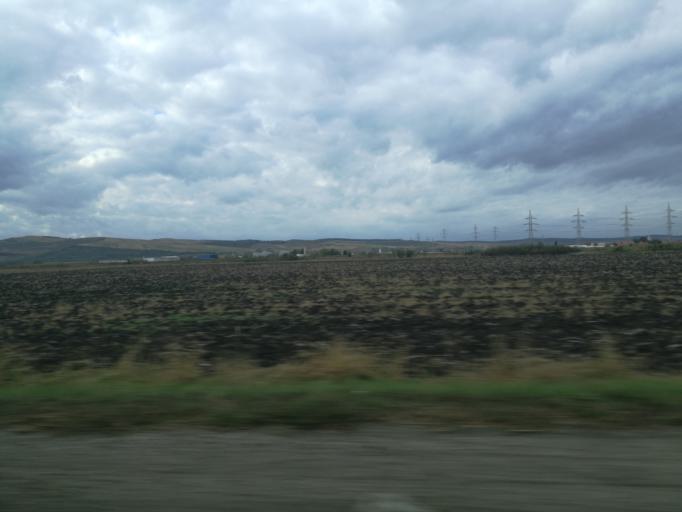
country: RO
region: Mures
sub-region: Comuna Cristesti
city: Cristesti
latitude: 46.4950
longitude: 24.4772
